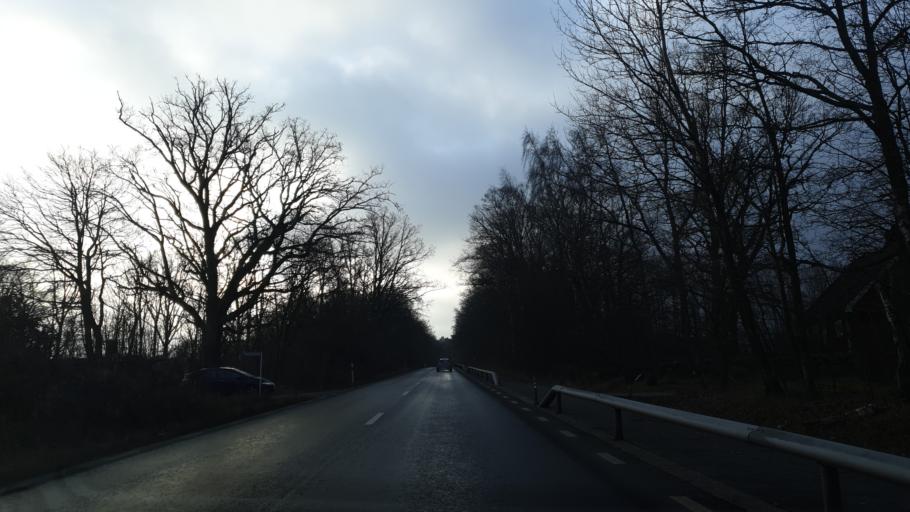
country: SE
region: Blekinge
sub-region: Karlshamns Kommun
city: Morrum
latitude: 56.1303
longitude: 14.6731
